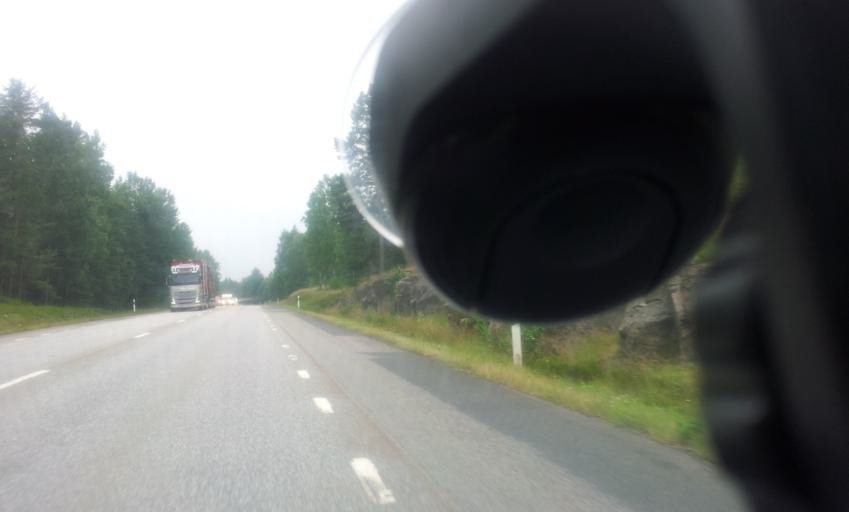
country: SE
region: Kalmar
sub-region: Vasterviks Kommun
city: Ankarsrum
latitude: 57.6974
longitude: 16.4417
